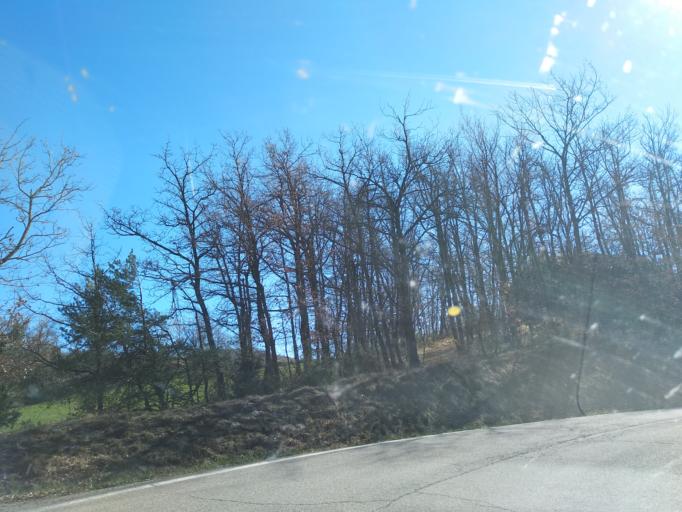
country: IT
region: Emilia-Romagna
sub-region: Provincia di Reggio Emilia
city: Castelnovo ne'Monti
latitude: 44.4032
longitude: 10.3972
